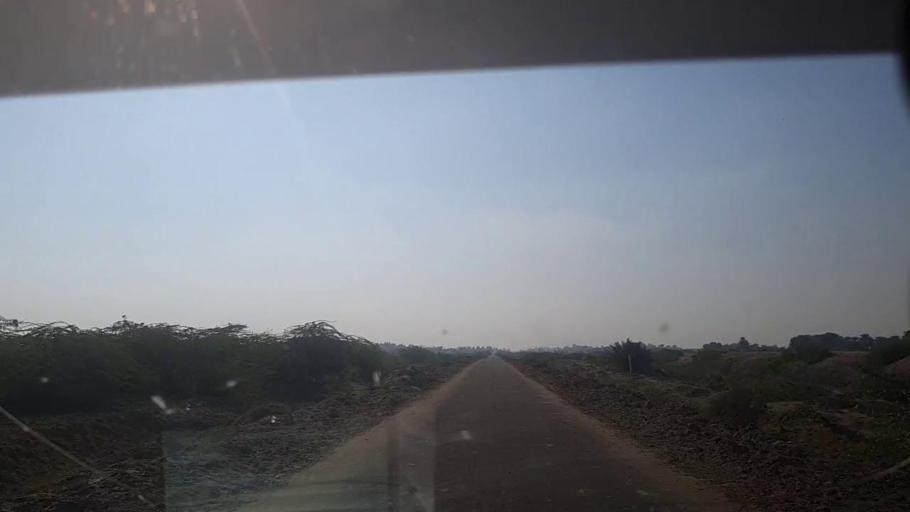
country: PK
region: Sindh
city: Gambat
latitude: 27.3829
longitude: 68.5860
